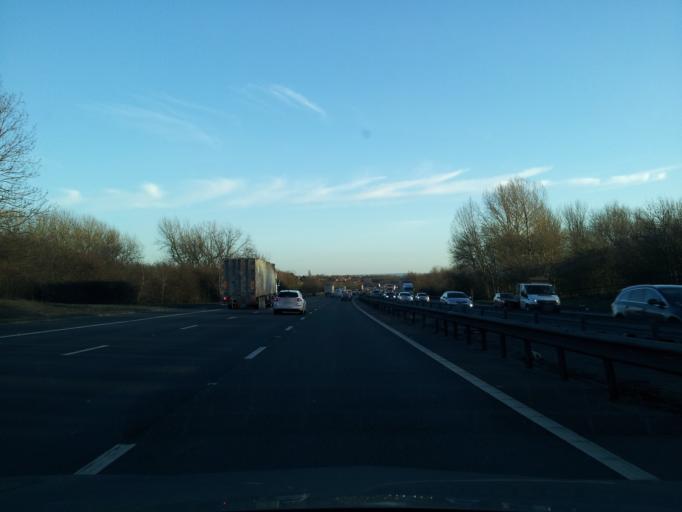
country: GB
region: England
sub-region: Milton Keynes
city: Gayhurst
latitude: 52.0967
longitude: -0.7618
